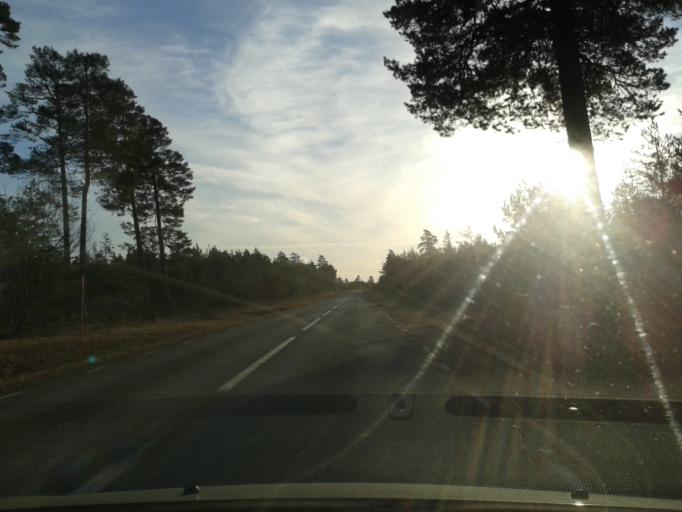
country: SE
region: Gotland
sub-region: Gotland
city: Hemse
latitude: 57.4044
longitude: 18.6371
